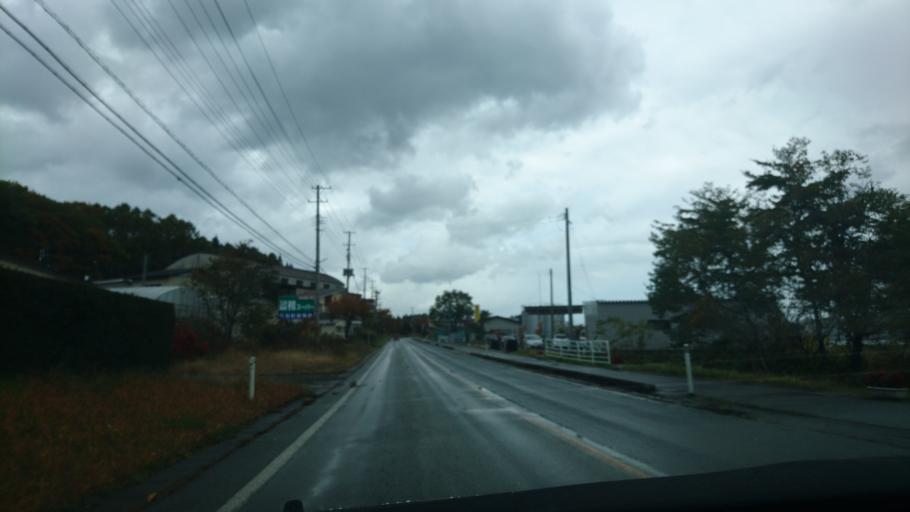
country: JP
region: Iwate
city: Shizukuishi
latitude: 39.6699
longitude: 140.9818
